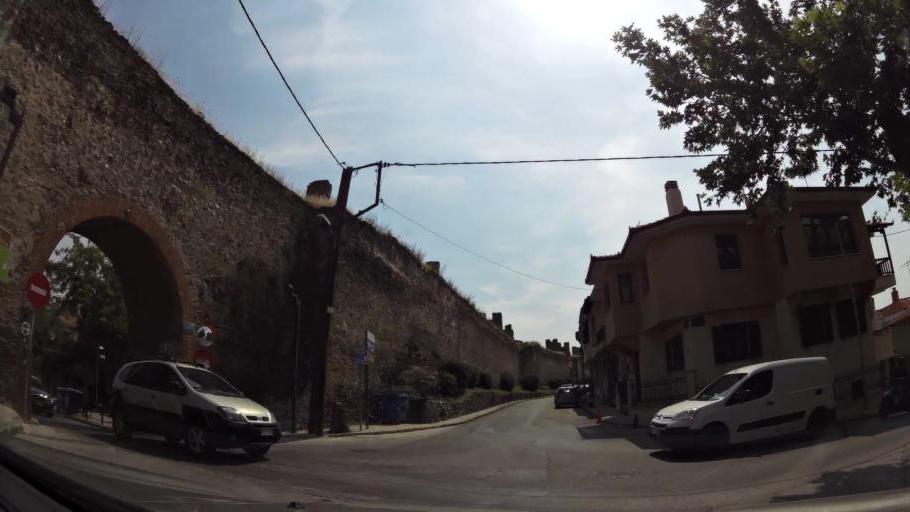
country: GR
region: Central Macedonia
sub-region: Nomos Thessalonikis
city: Agios Pavlos
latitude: 40.6422
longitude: 22.9555
